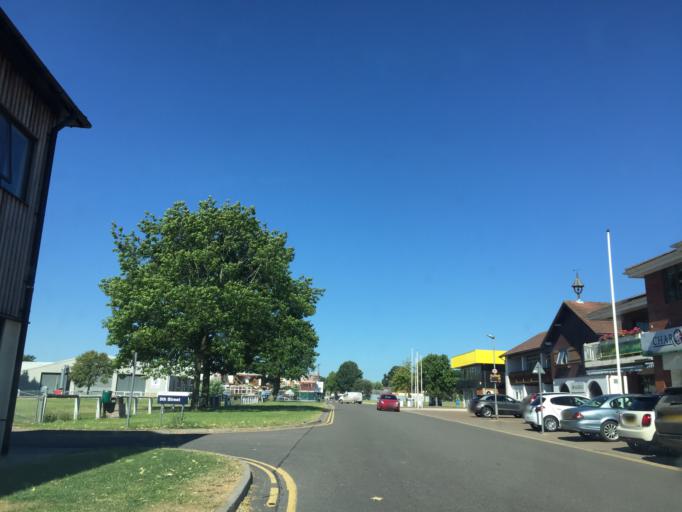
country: GB
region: England
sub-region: Warwickshire
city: Royal Leamington Spa
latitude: 52.3395
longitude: -1.5234
